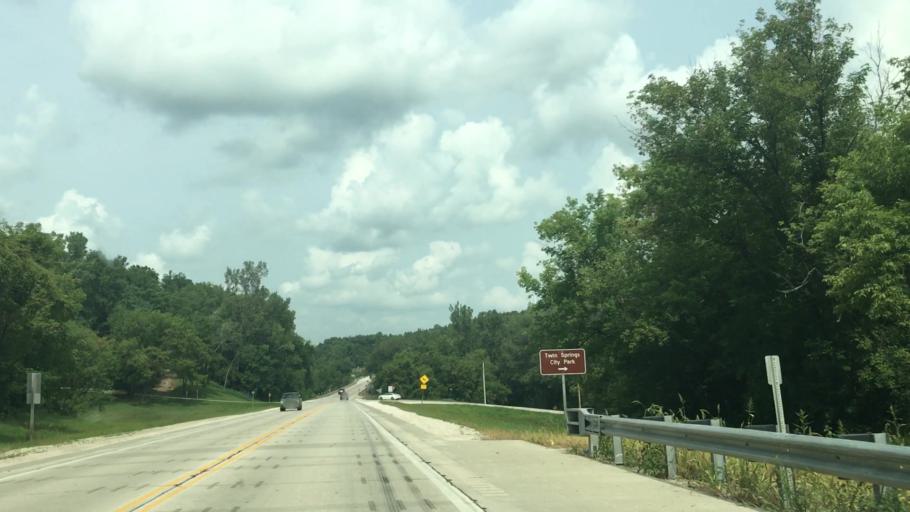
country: US
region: Iowa
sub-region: Winneshiek County
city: Decorah
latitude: 43.2961
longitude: -91.8091
